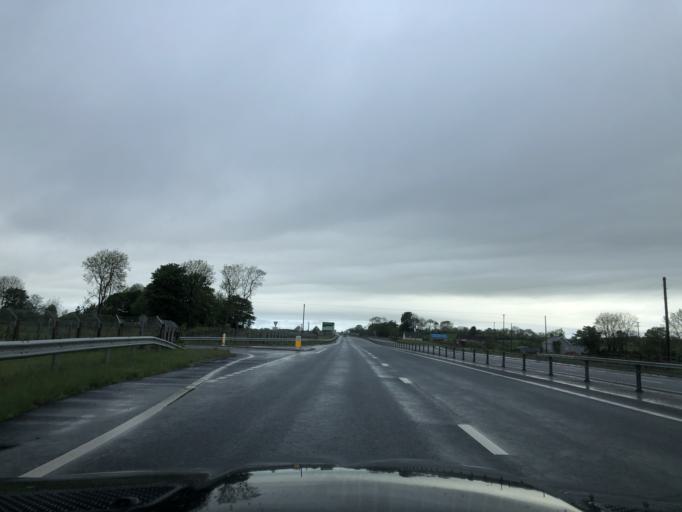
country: GB
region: Northern Ireland
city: Dunloy
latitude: 54.9946
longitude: -6.3519
